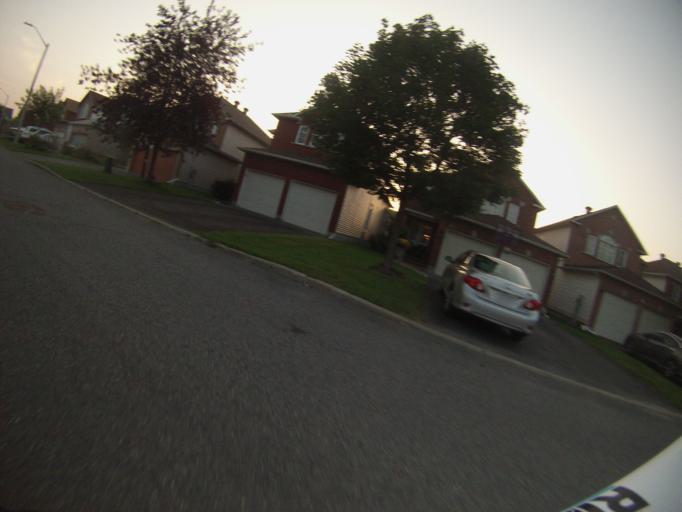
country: CA
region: Ontario
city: Ottawa
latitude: 45.3704
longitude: -75.6274
